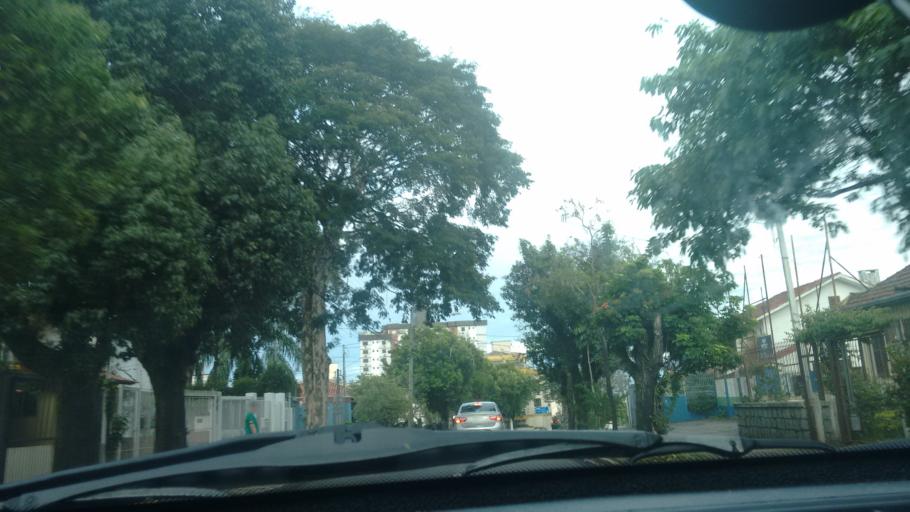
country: BR
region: Rio Grande do Sul
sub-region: Porto Alegre
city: Porto Alegre
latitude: -30.0087
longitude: -51.1608
